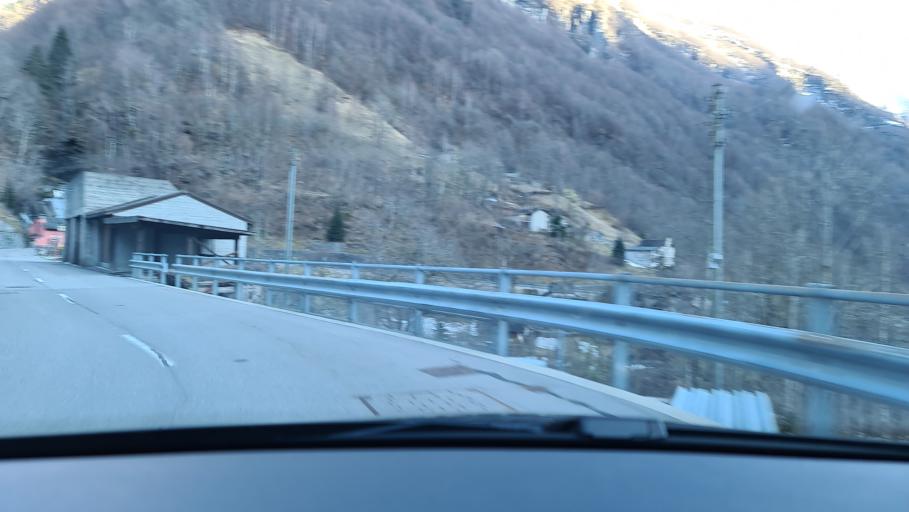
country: CH
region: Ticino
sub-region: Locarno District
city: Lavertezzo
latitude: 46.3382
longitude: 8.8040
